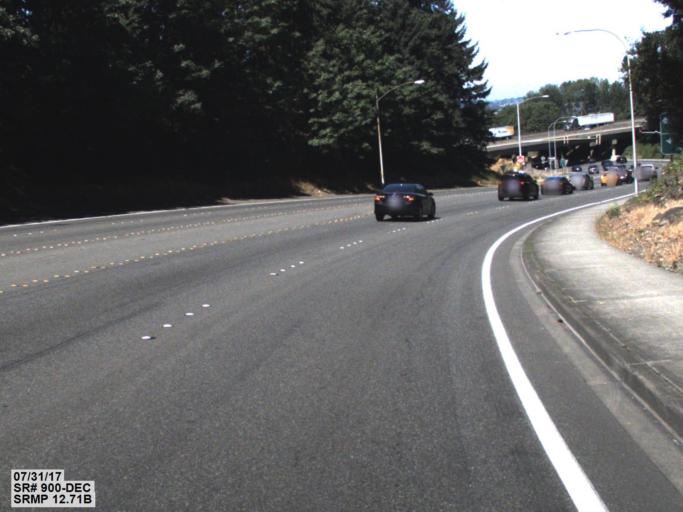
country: US
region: Washington
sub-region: King County
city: Renton
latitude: 47.5011
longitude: -122.1931
